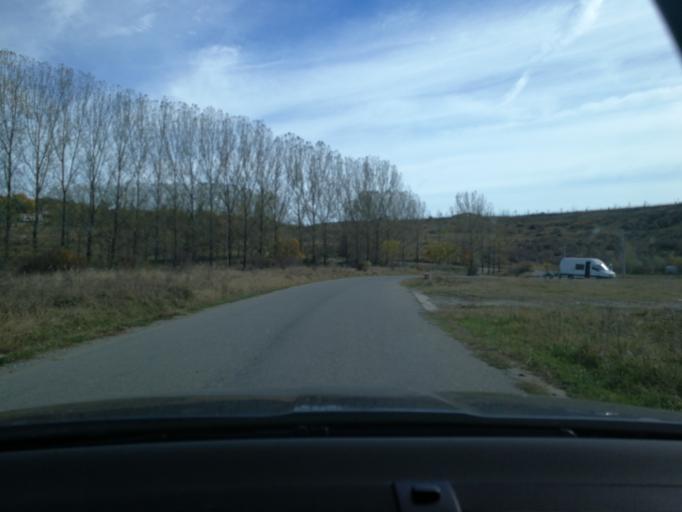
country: RO
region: Prahova
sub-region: Comuna Cornu
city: Cornu de Jos
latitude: 45.1485
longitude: 25.7249
